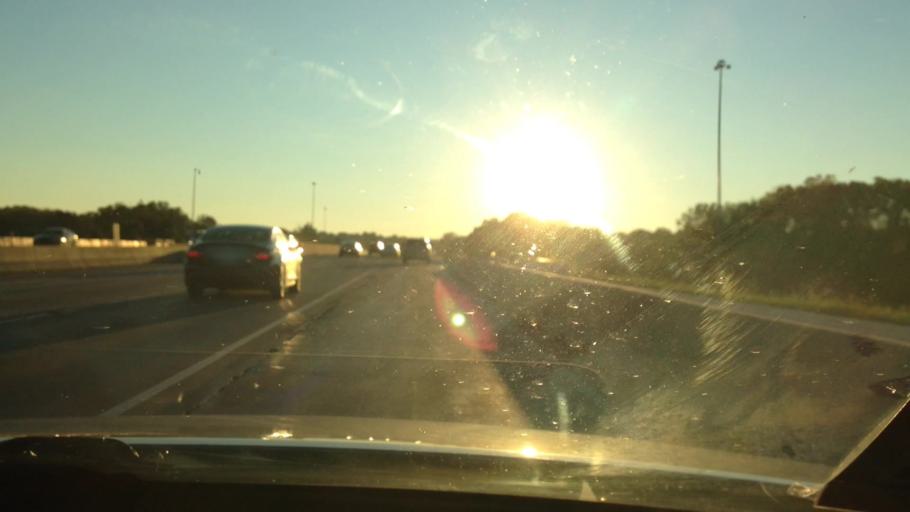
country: US
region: Kansas
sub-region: Johnson County
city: Leawood
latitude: 38.9377
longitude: -94.6063
